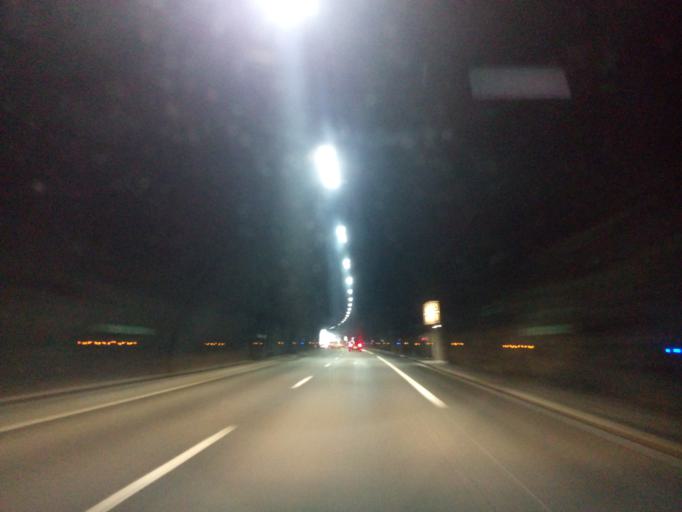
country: FR
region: Rhone-Alpes
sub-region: Departement de la Savoie
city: La Bridoire
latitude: 45.5571
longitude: 5.7336
